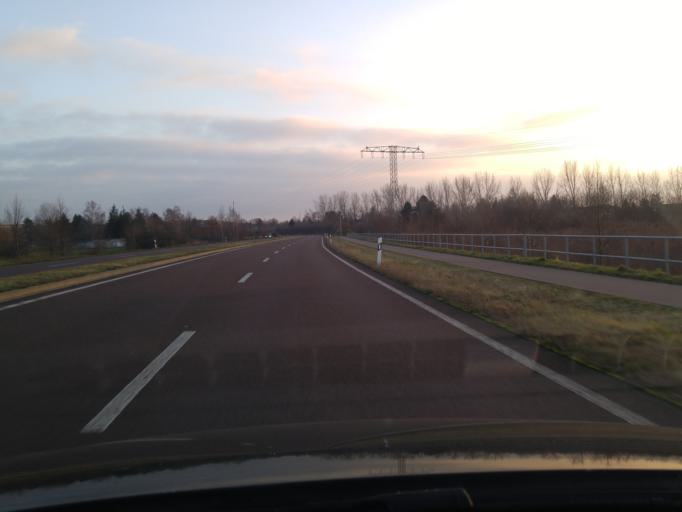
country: DE
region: Saxony
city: Leipzig
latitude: 51.3808
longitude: 12.3425
